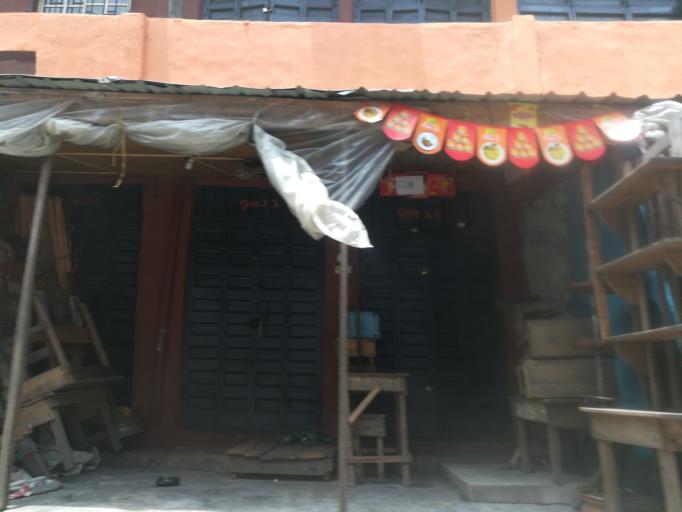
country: NG
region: Lagos
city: Lagos
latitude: 6.4625
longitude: 3.3852
